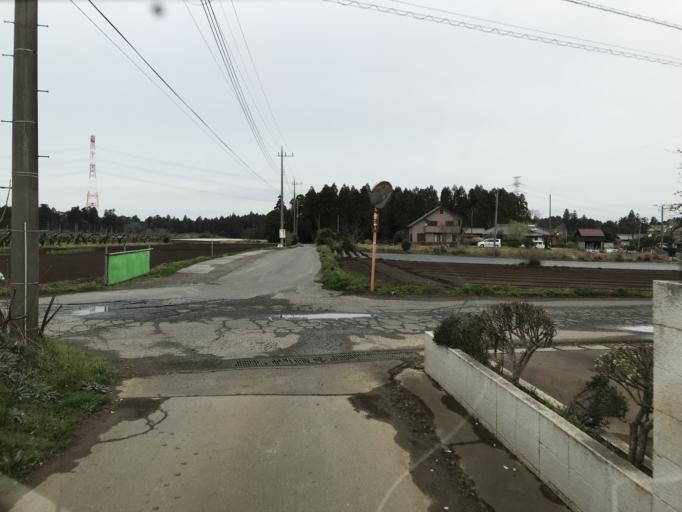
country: JP
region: Chiba
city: Sawara
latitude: 35.8590
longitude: 140.5099
